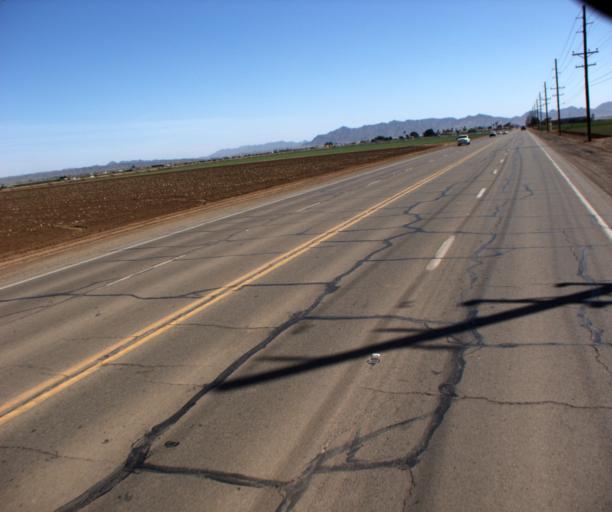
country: US
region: Arizona
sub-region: Yuma County
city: Yuma
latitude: 32.6990
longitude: -114.5418
